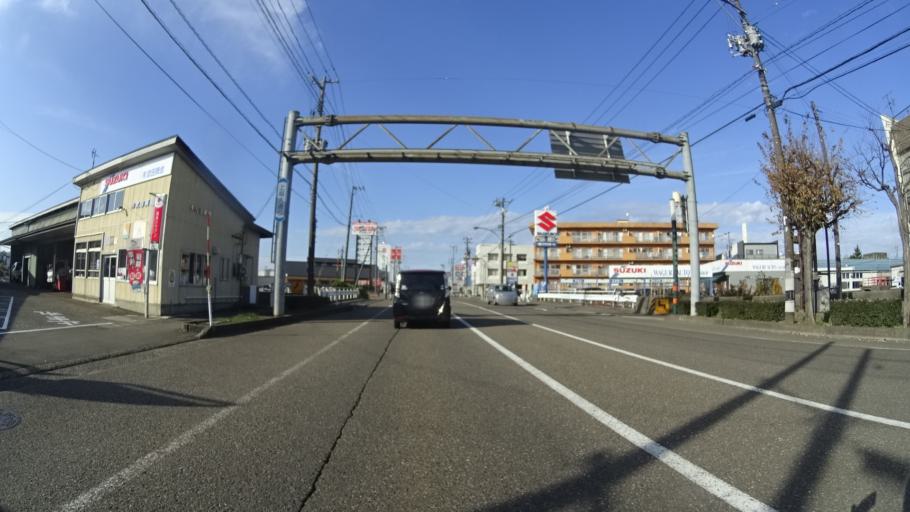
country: JP
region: Niigata
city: Joetsu
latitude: 37.1274
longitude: 138.2481
